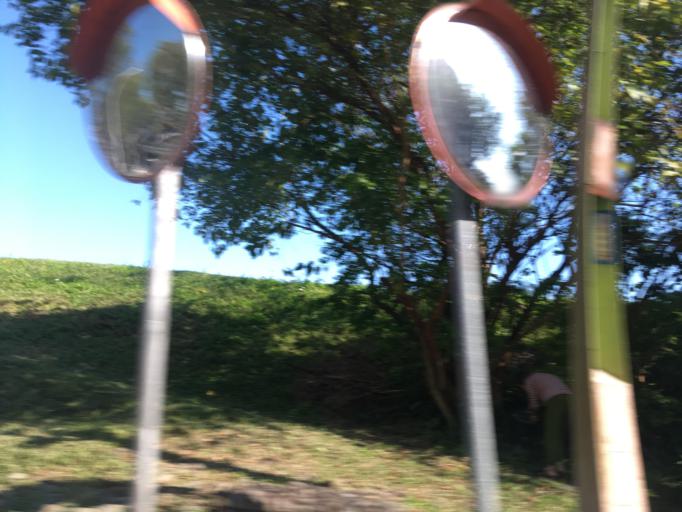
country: TW
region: Taiwan
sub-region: Yilan
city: Yilan
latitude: 24.7636
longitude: 121.7584
